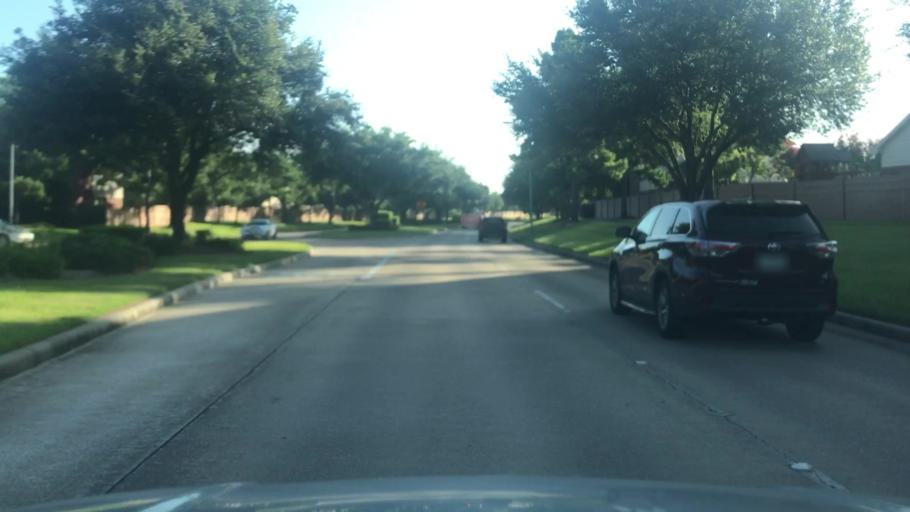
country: US
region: Texas
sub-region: Fort Bend County
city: Cinco Ranch
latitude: 29.7474
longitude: -95.7878
